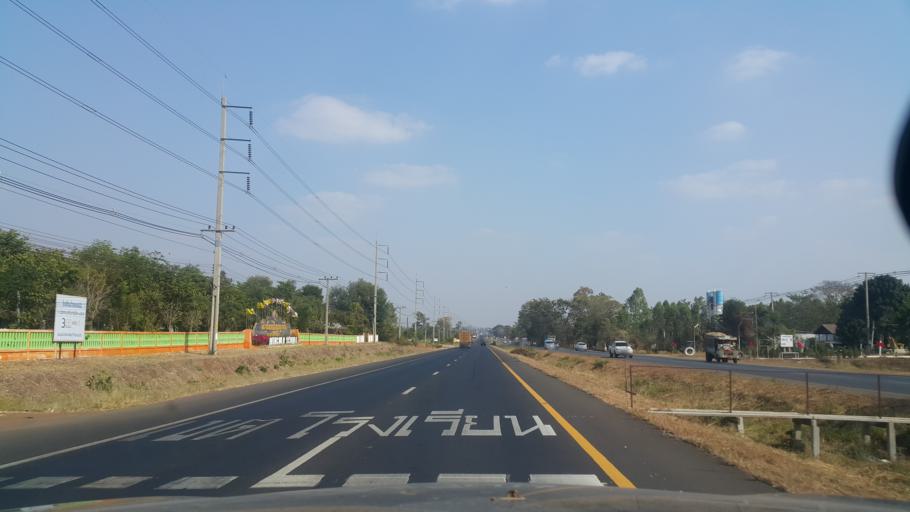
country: TH
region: Buriram
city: Nong Ki
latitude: 14.7042
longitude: 102.4790
